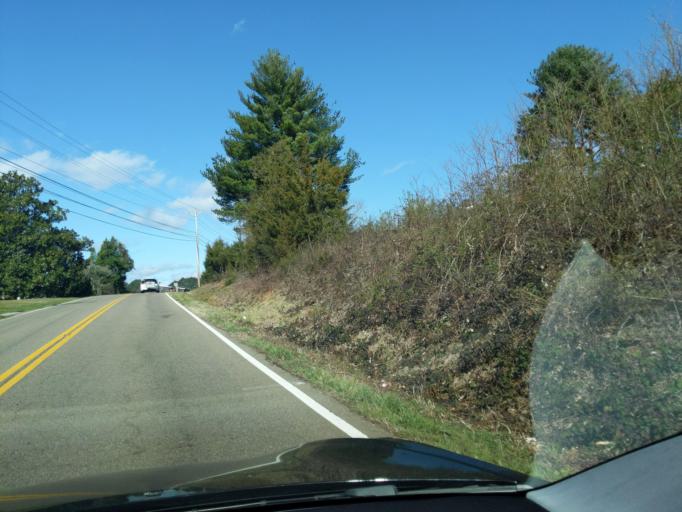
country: US
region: Tennessee
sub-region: Jefferson County
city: Dandridge
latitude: 35.9703
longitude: -83.5131
